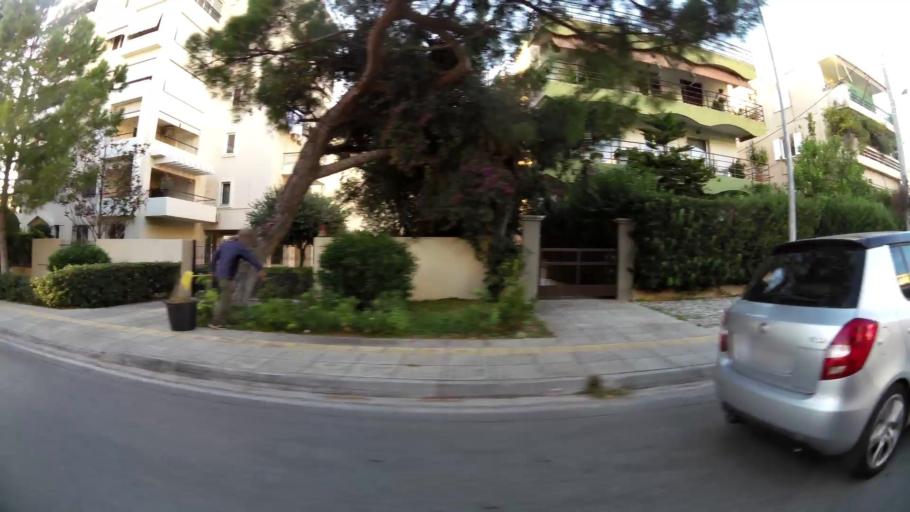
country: GR
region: Attica
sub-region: Nomarchia Athinas
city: Glyfada
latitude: 37.8708
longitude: 23.7527
